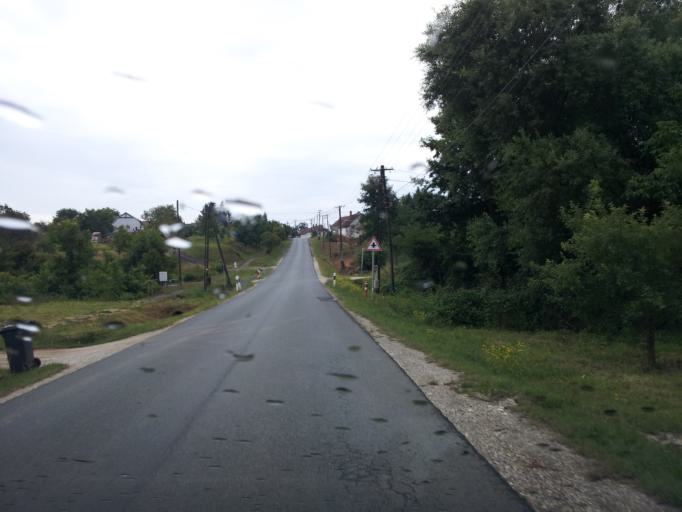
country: HU
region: Vas
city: Kormend
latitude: 46.9643
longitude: 16.6164
